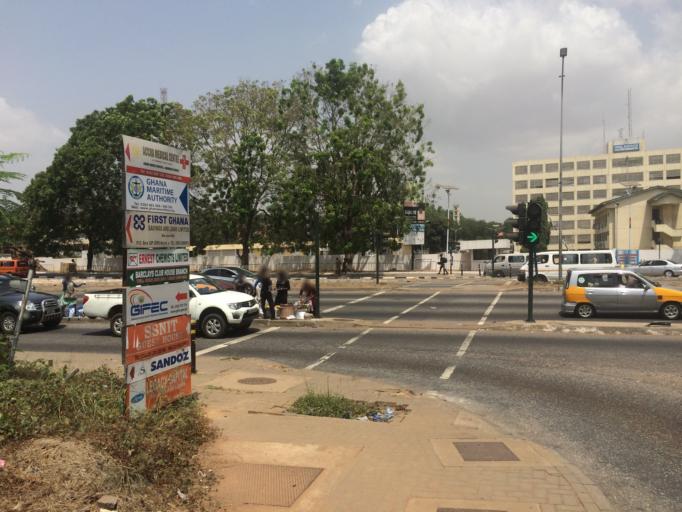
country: GH
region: Greater Accra
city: Accra
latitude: 5.5704
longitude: -0.1878
